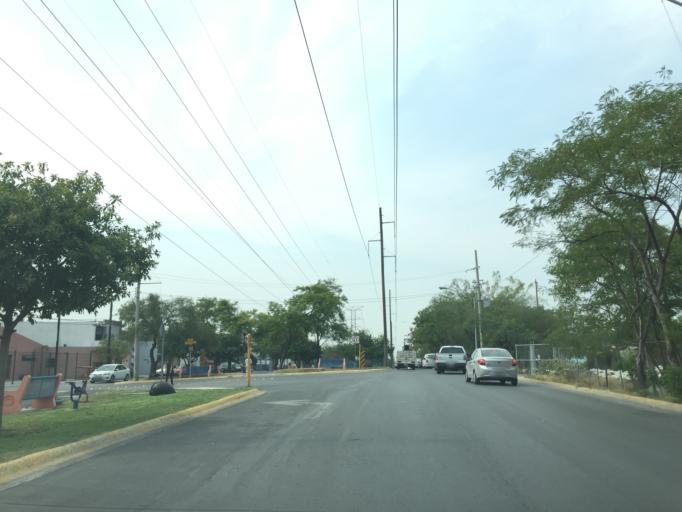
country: MX
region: Nuevo Leon
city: Guadalupe
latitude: 25.7201
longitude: -100.2212
